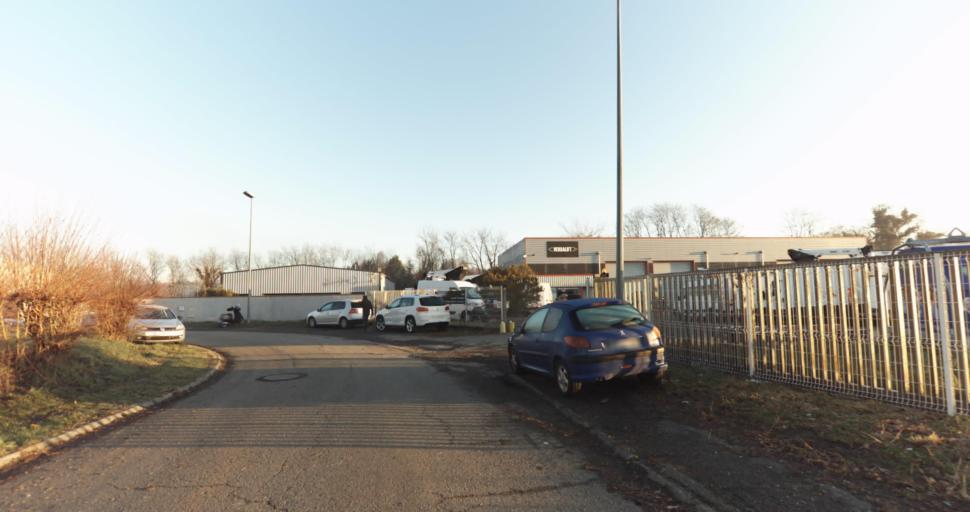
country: FR
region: Aquitaine
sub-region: Departement des Pyrenees-Atlantiques
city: Buros
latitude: 43.3237
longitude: -0.2940
